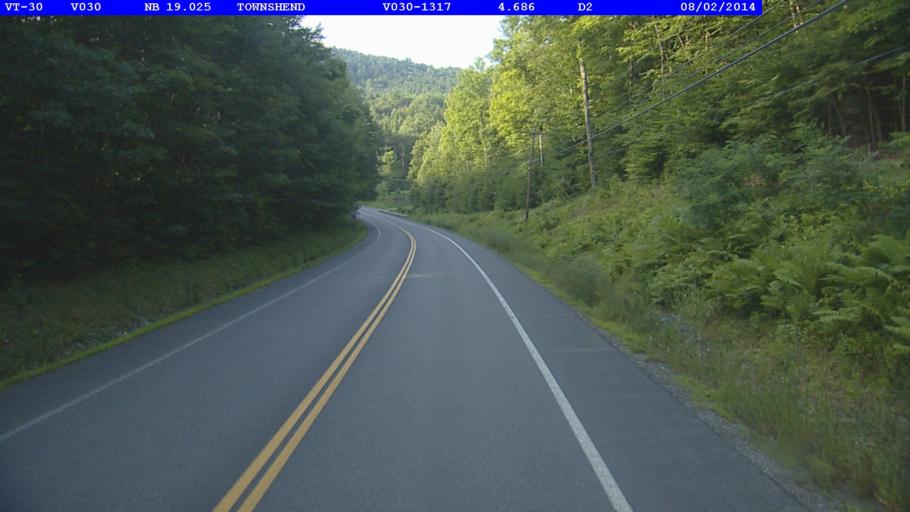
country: US
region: Vermont
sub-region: Windham County
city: Newfane
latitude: 43.0619
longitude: -72.6975
